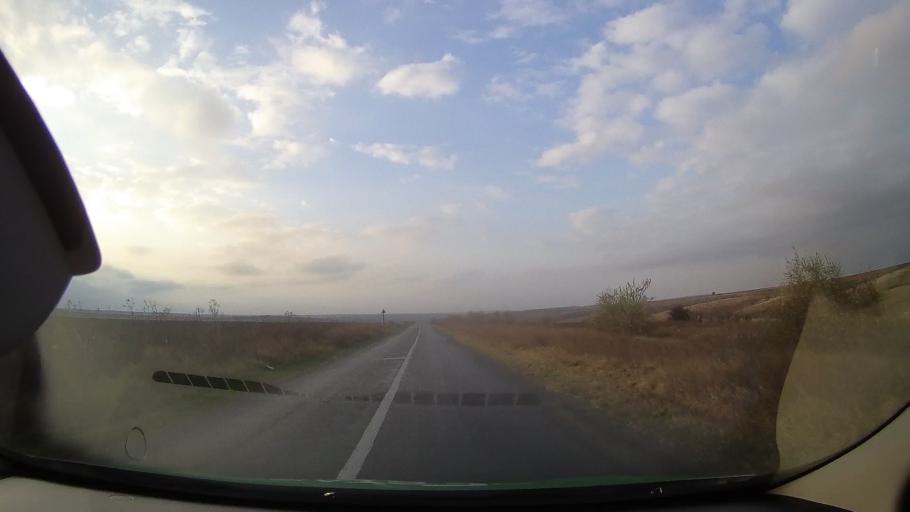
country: RO
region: Constanta
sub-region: Comuna Adamclisi
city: Adamclisi
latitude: 44.0173
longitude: 27.8915
